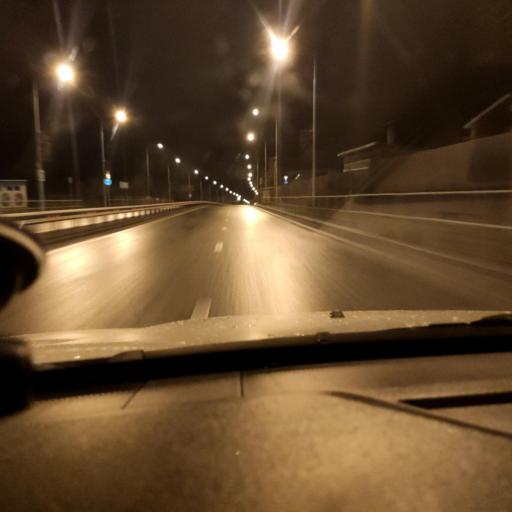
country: RU
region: Samara
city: Petra-Dubrava
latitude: 53.2977
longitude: 50.2443
